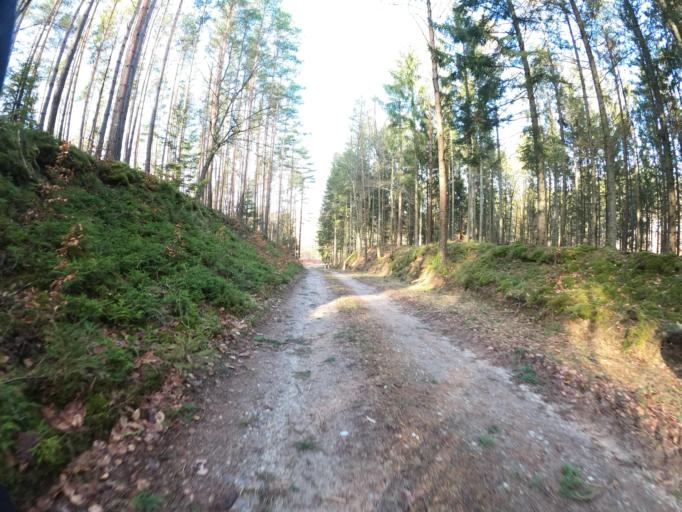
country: PL
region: West Pomeranian Voivodeship
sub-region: Powiat koszalinski
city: Polanow
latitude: 54.2285
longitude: 16.6854
